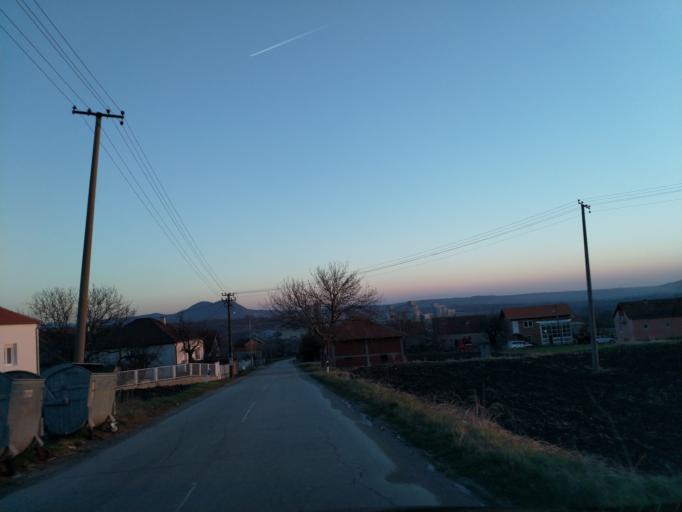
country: RS
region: Central Serbia
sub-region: Pomoravski Okrug
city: Paracin
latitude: 43.9219
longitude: 21.5104
